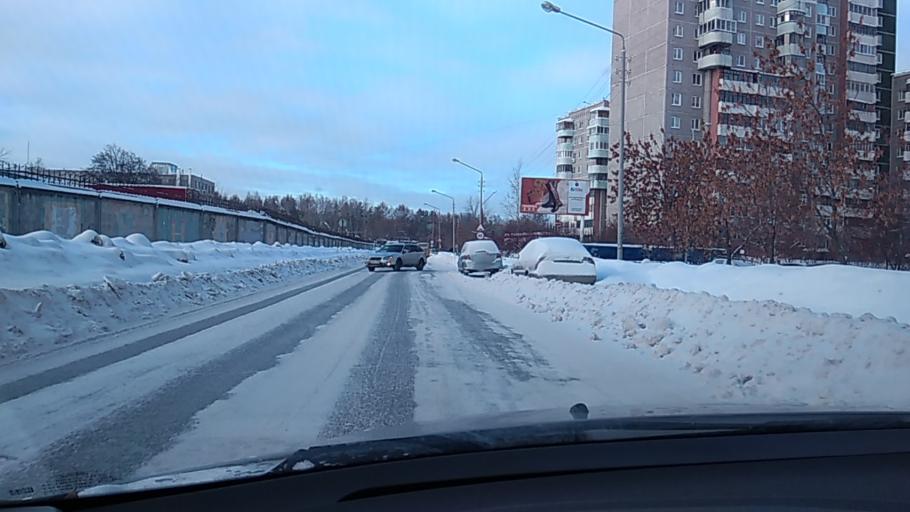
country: RU
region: Sverdlovsk
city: Yekaterinburg
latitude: 56.7924
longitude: 60.6105
